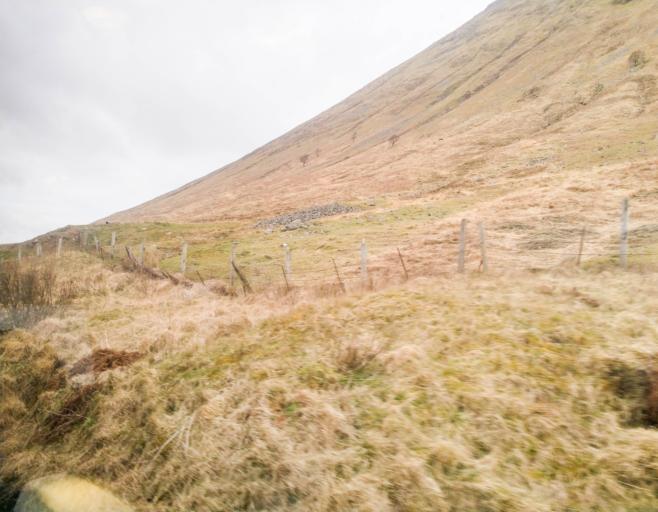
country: GB
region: Scotland
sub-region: Argyll and Bute
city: Garelochhead
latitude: 56.4896
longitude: -4.7285
